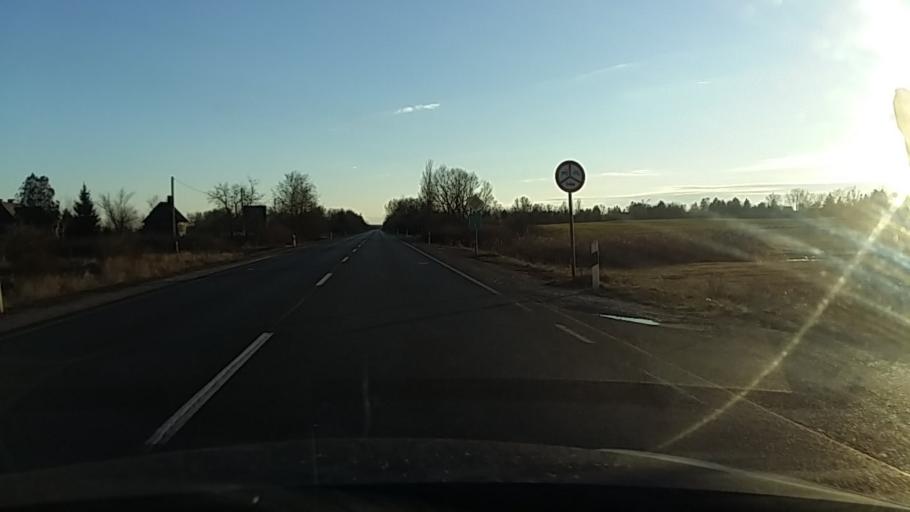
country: HU
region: Szabolcs-Szatmar-Bereg
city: Ujfeherto
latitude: 47.8702
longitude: 21.7053
